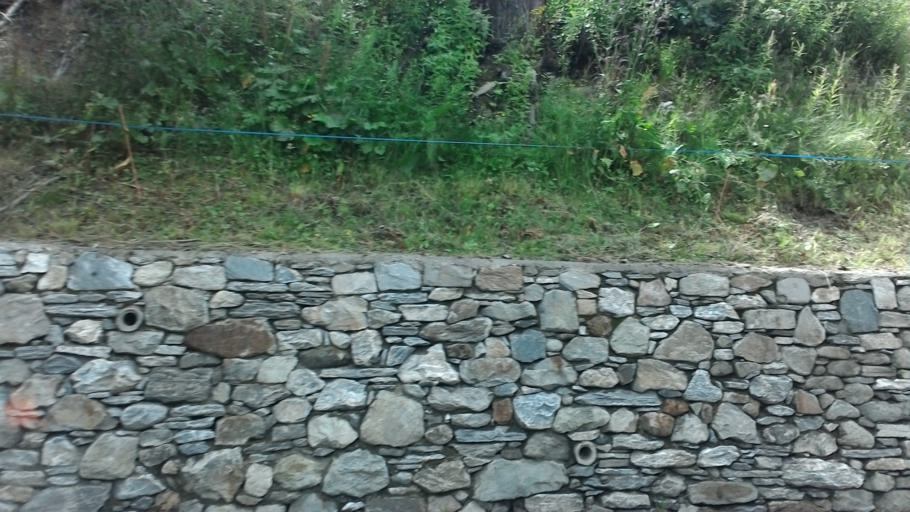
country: IT
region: Aosta Valley
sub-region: Valle d'Aosta
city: La Thuile
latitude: 45.7094
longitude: 6.9342
